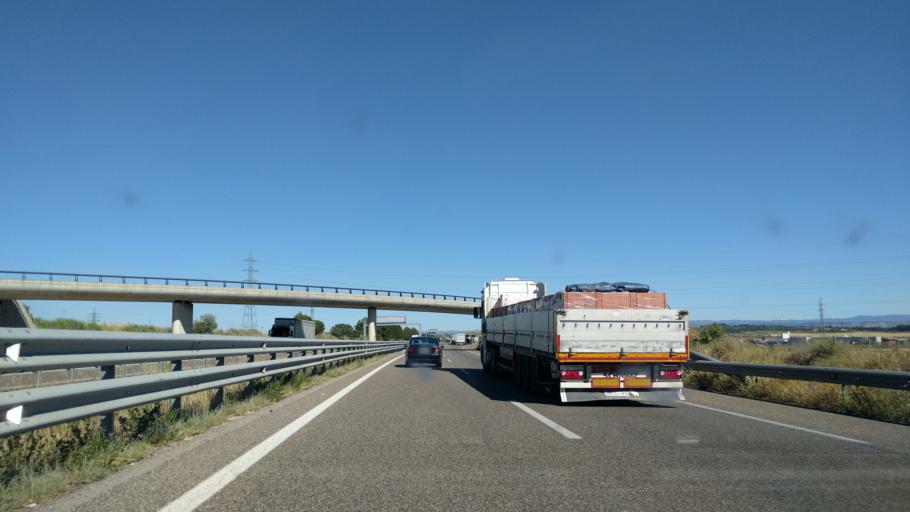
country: ES
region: Catalonia
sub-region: Provincia de Lleida
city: Alcoletge
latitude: 41.6351
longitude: 0.6891
